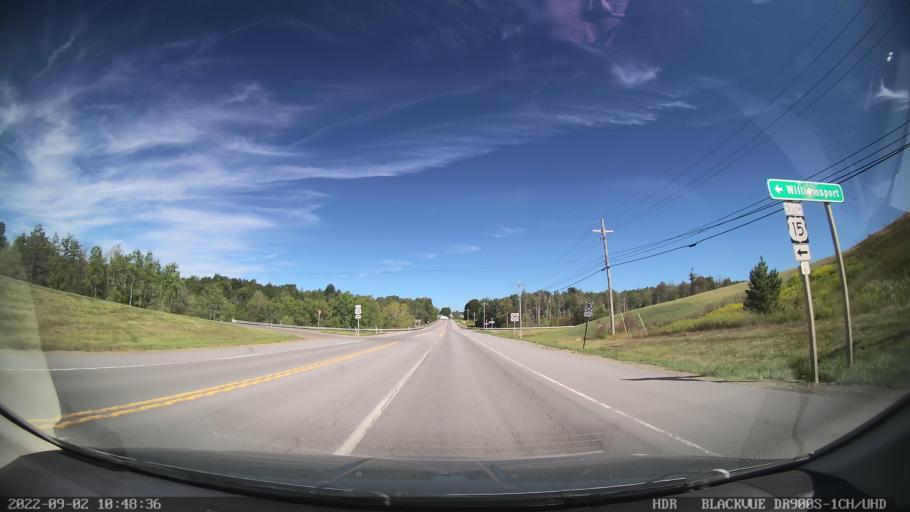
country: US
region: Pennsylvania
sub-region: Tioga County
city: Blossburg
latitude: 41.5894
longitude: -77.1088
